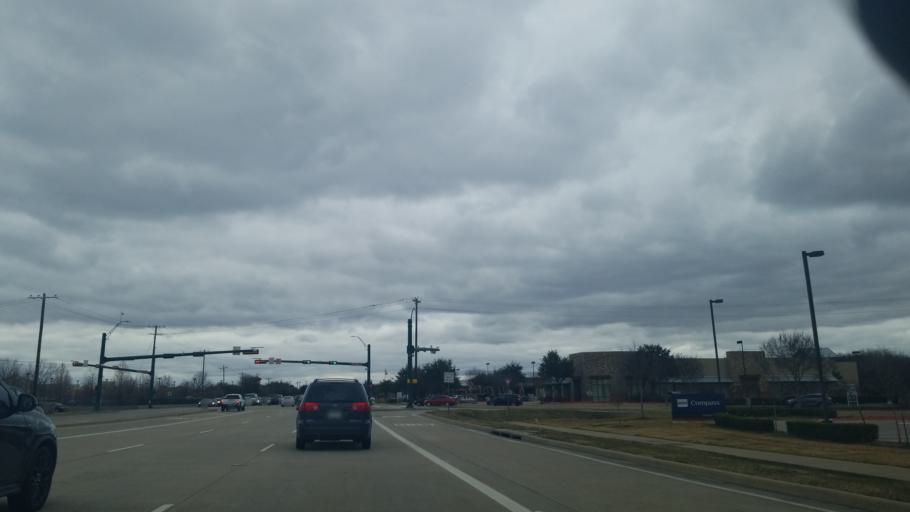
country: US
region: Texas
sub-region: Denton County
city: Double Oak
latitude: 33.0657
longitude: -97.0803
